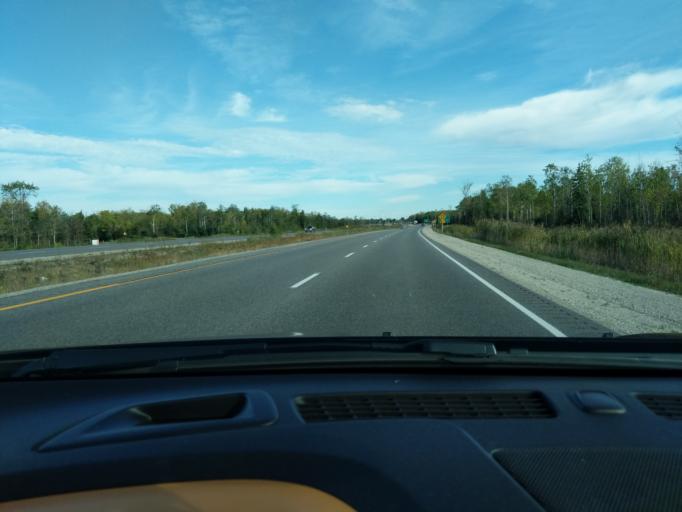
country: CA
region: Ontario
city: Collingwood
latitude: 44.4643
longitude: -80.1219
